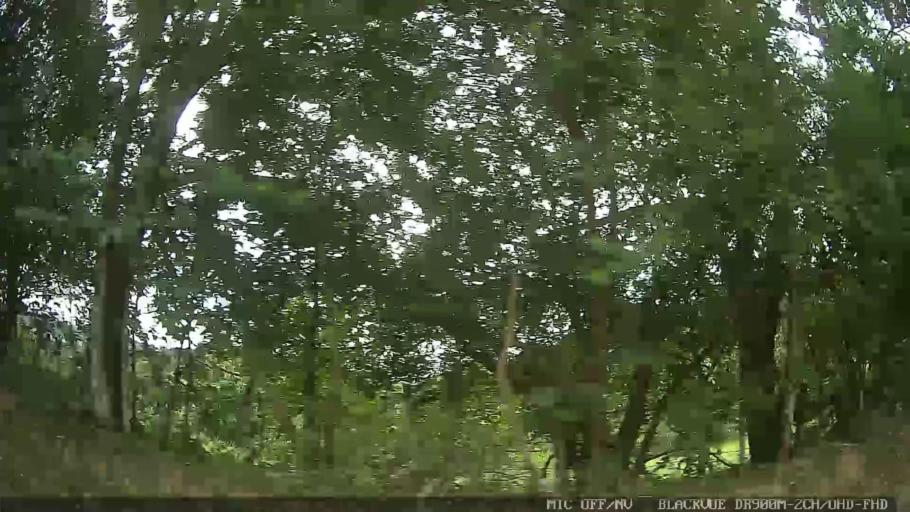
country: BR
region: Sao Paulo
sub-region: Atibaia
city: Atibaia
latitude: -23.1528
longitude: -46.5619
